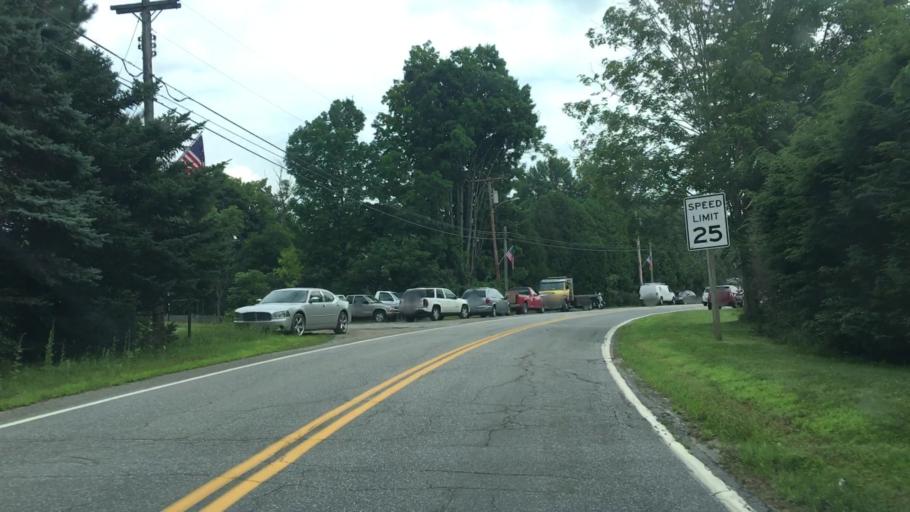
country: US
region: Maine
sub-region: Kennebec County
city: Vassalboro
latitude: 44.4510
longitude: -69.6068
